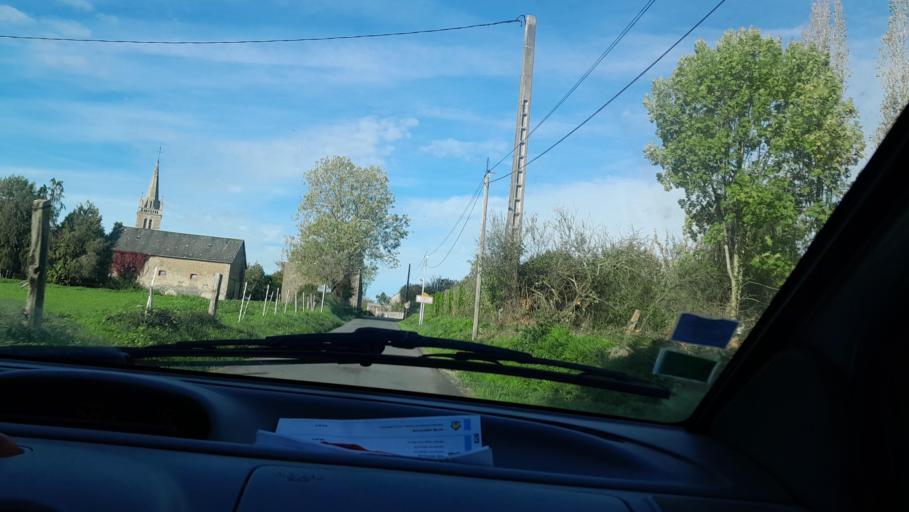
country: FR
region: Lower Normandy
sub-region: Departement de la Manche
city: Pontorson
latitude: 48.5609
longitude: -1.4630
